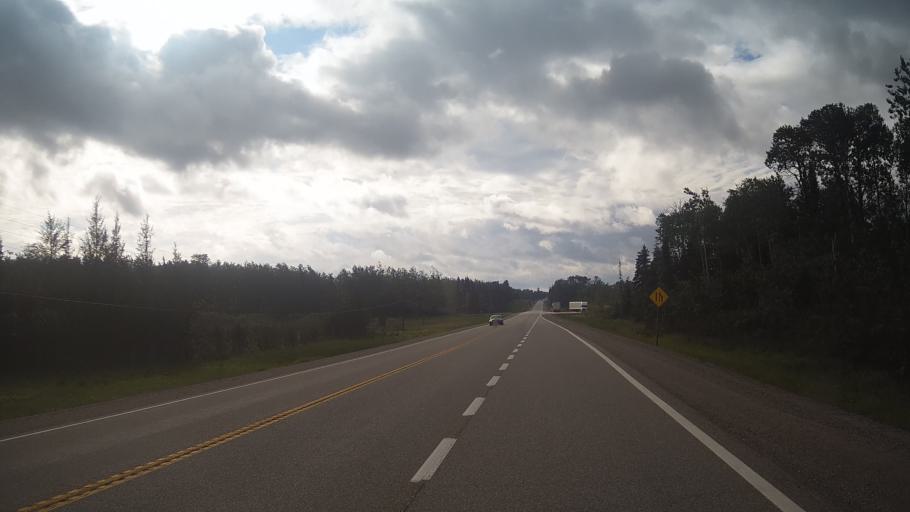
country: CA
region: Ontario
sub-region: Rainy River District
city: Atikokan
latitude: 49.0079
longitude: -90.4174
